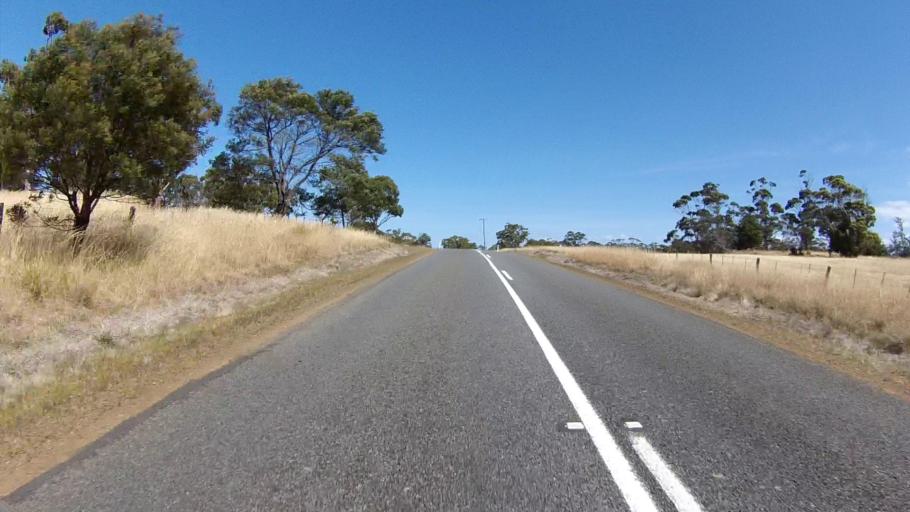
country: AU
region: Tasmania
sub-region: Sorell
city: Sorell
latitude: -42.2820
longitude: 147.9990
